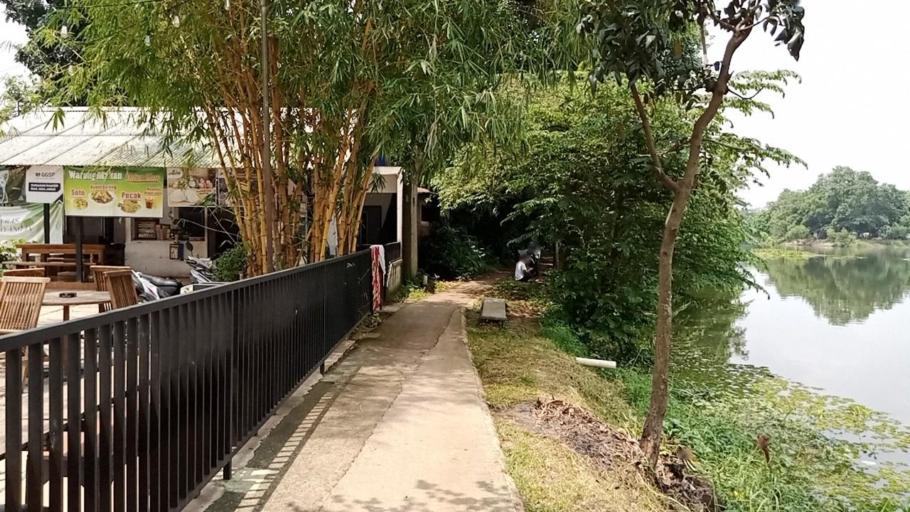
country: ID
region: West Java
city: Sawangan
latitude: -6.3851
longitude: 106.7539
